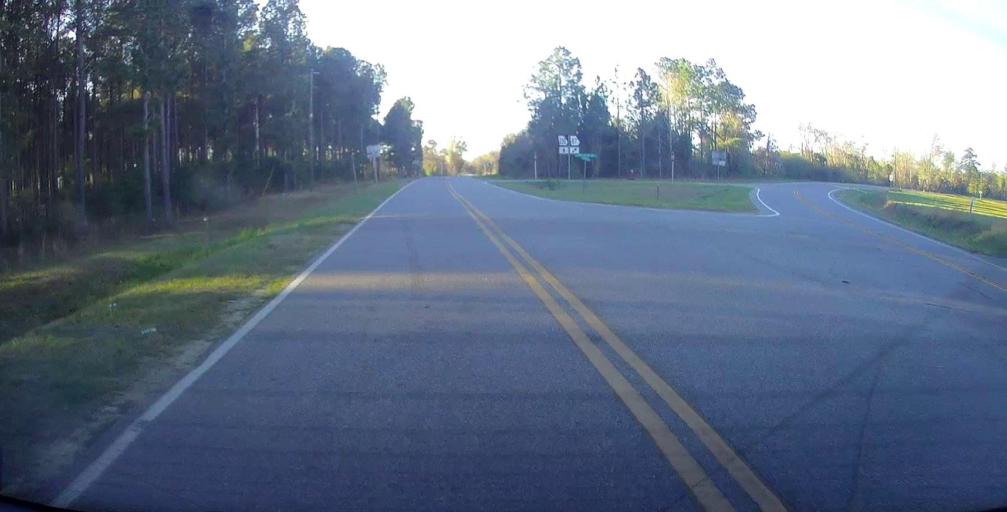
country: US
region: Georgia
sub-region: Wilcox County
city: Abbeville
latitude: 32.0616
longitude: -83.2731
